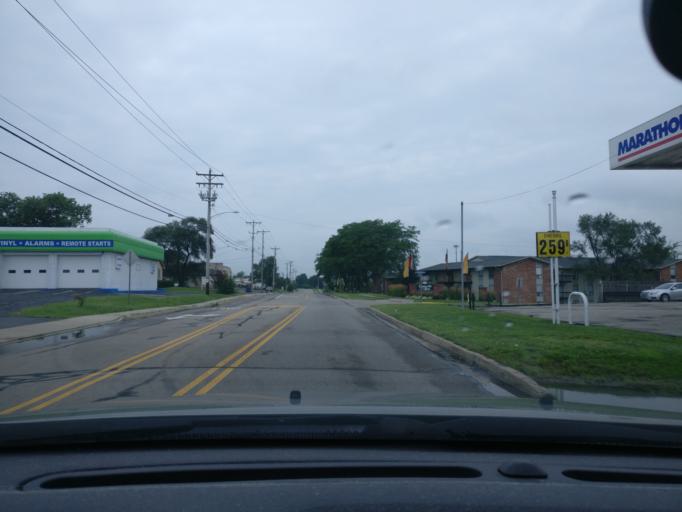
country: US
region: Ohio
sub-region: Montgomery County
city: West Carrollton City
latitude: 39.6406
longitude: -84.2356
